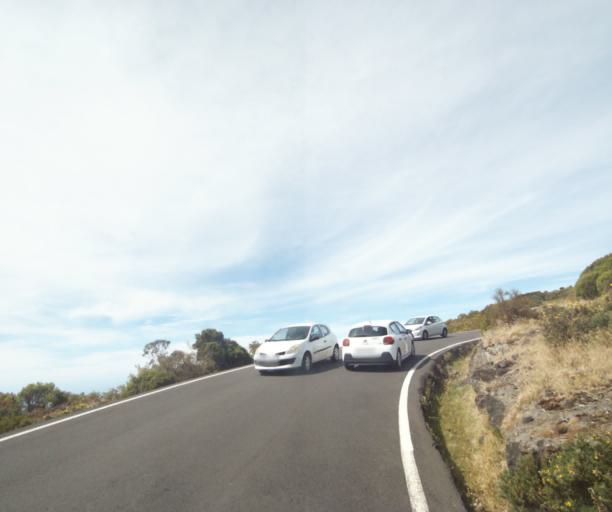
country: RE
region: Reunion
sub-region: Reunion
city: Trois-Bassins
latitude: -21.0697
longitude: 55.3845
